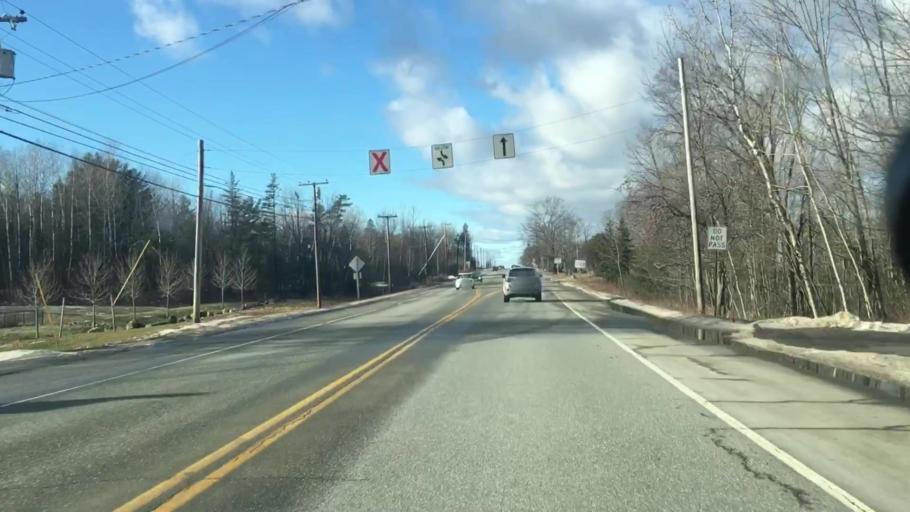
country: US
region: Maine
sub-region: Penobscot County
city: Holden
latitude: 44.7615
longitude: -68.6982
